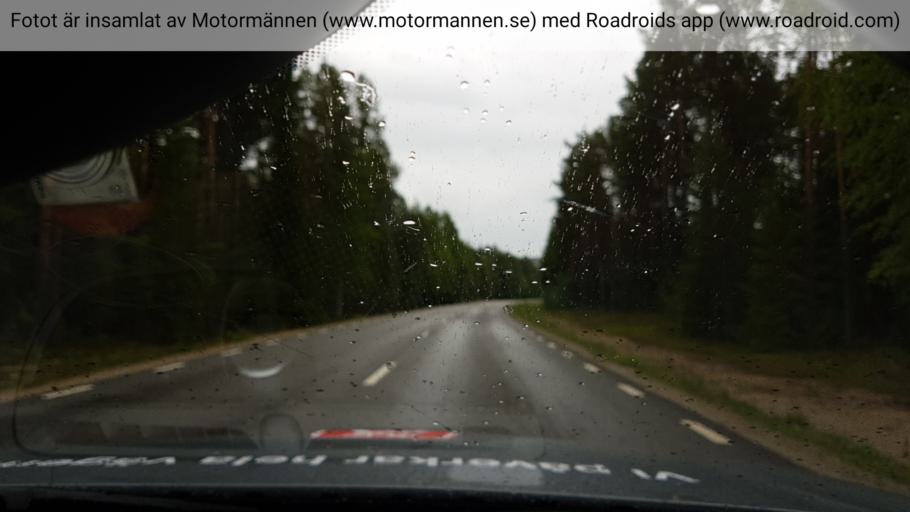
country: SE
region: Jaemtland
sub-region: Bergs Kommun
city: Hoverberg
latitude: 62.4979
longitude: 14.7076
